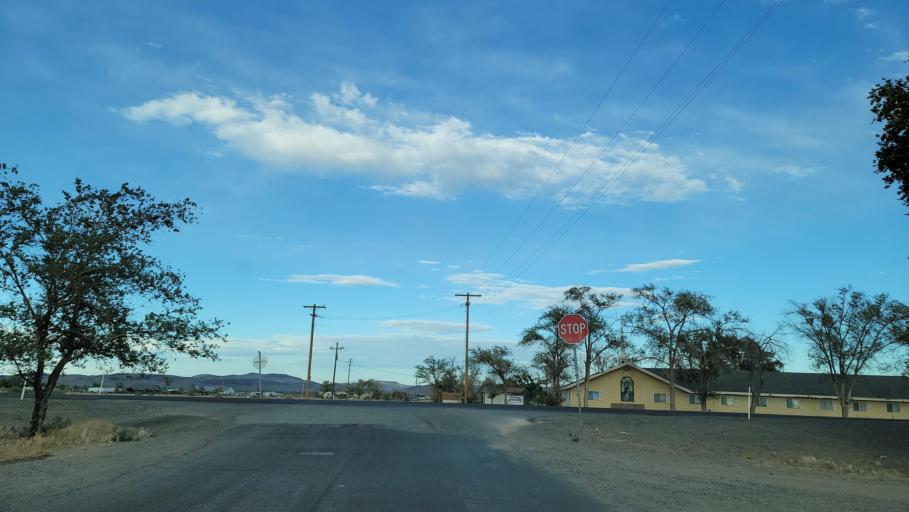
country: US
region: Nevada
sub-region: Lyon County
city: Silver Springs
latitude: 39.4007
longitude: -119.2287
